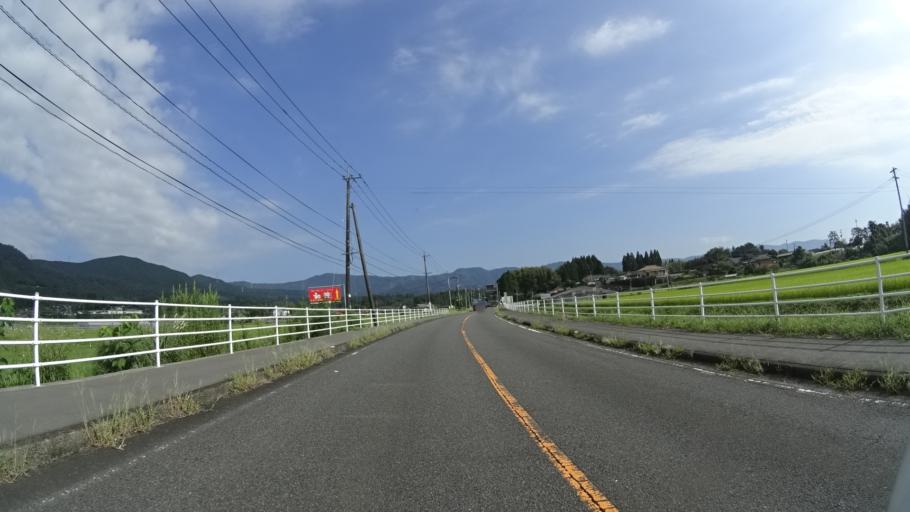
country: JP
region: Kagoshima
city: Okuchi-shinohara
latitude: 32.0320
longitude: 130.7435
